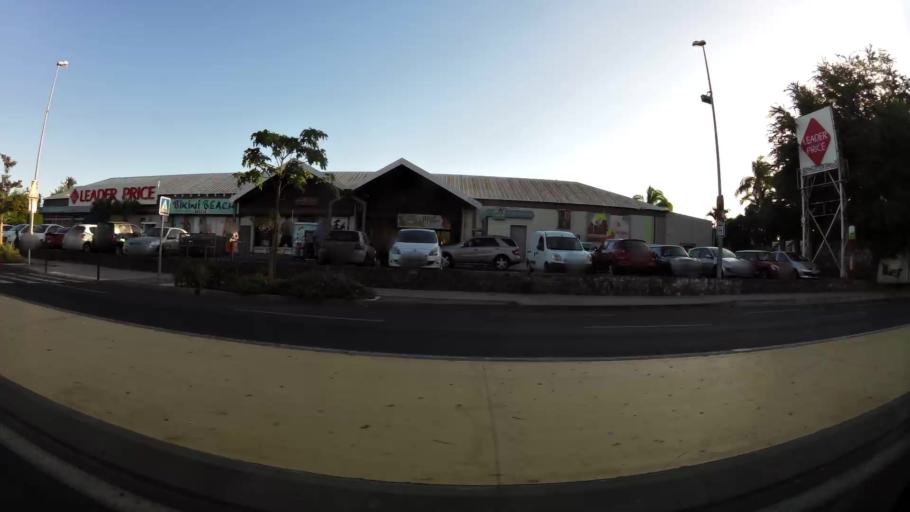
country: RE
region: Reunion
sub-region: Reunion
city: Trois-Bassins
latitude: -21.0843
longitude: 55.2317
